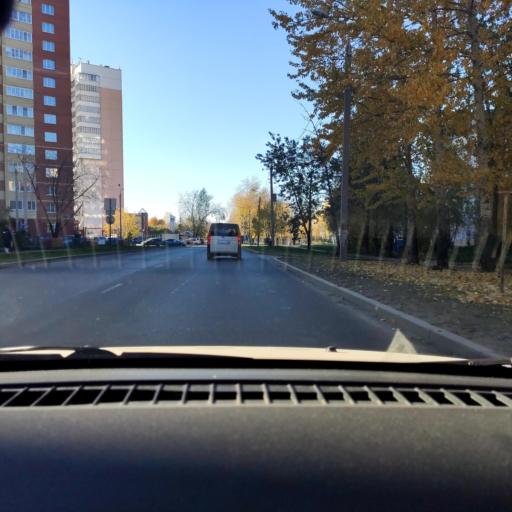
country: RU
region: Perm
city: Perm
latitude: 58.0629
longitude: 56.3579
